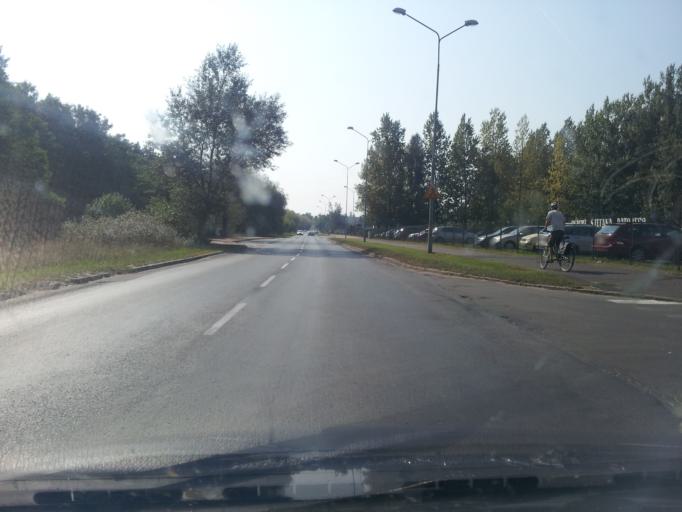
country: PL
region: Greater Poland Voivodeship
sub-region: Poznan
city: Poznan
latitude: 52.4578
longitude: 16.9276
